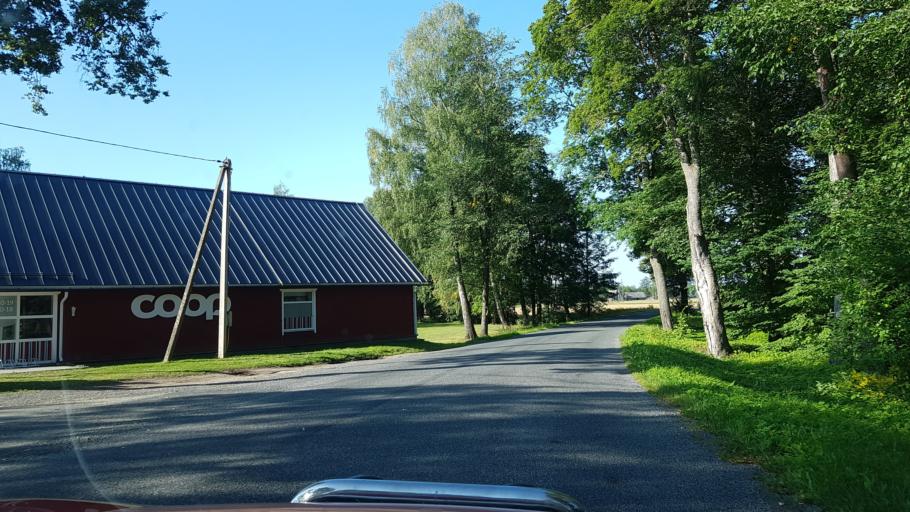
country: EE
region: Vorumaa
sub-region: Antsla vald
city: Vana-Antsla
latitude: 57.7423
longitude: 26.6522
